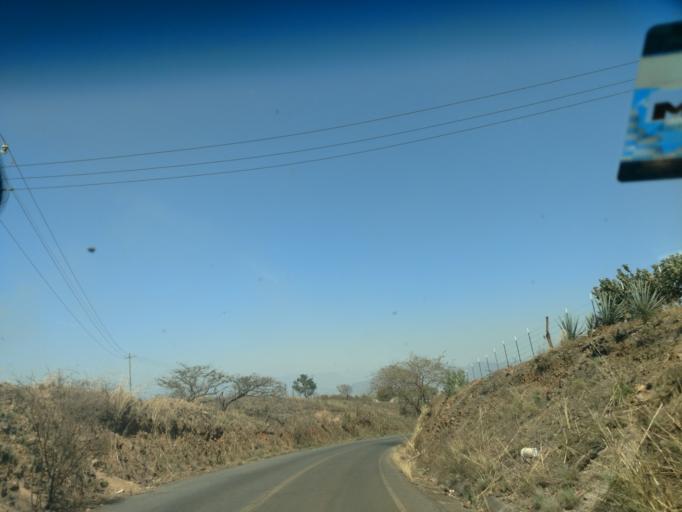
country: MX
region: Nayarit
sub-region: Tepic
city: La Corregidora
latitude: 21.4929
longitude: -104.6867
